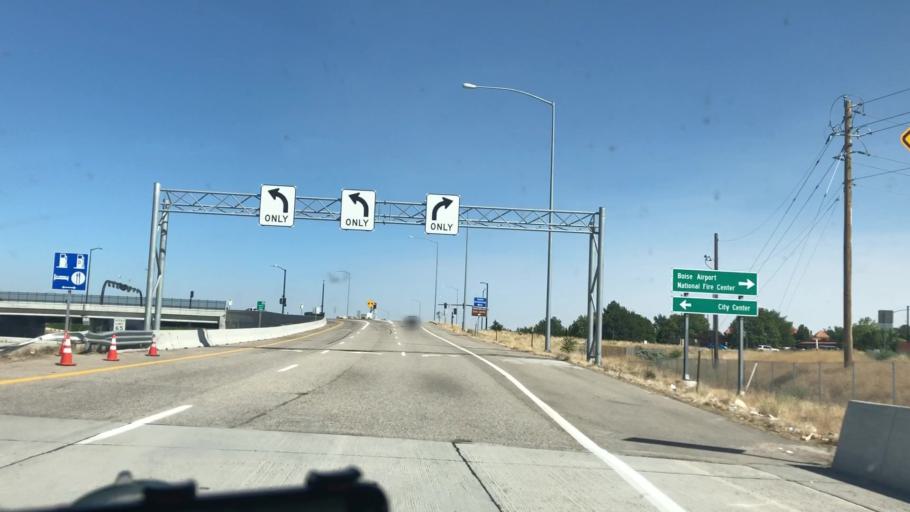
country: US
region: Idaho
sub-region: Ada County
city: Boise
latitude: 43.5714
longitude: -116.2181
